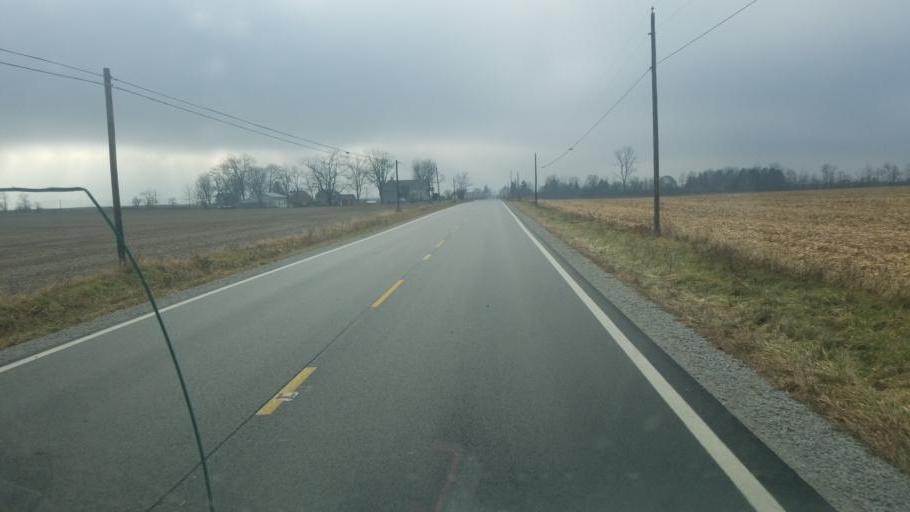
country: US
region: Ohio
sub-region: Hardin County
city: Forest
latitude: 40.6900
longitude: -83.4885
